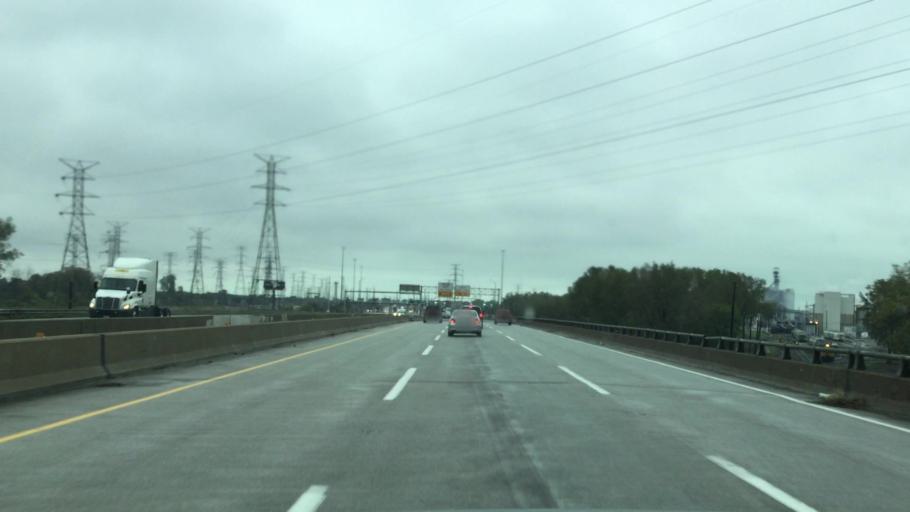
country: US
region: Indiana
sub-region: Lake County
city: Whiting
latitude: 41.6817
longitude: -87.5223
